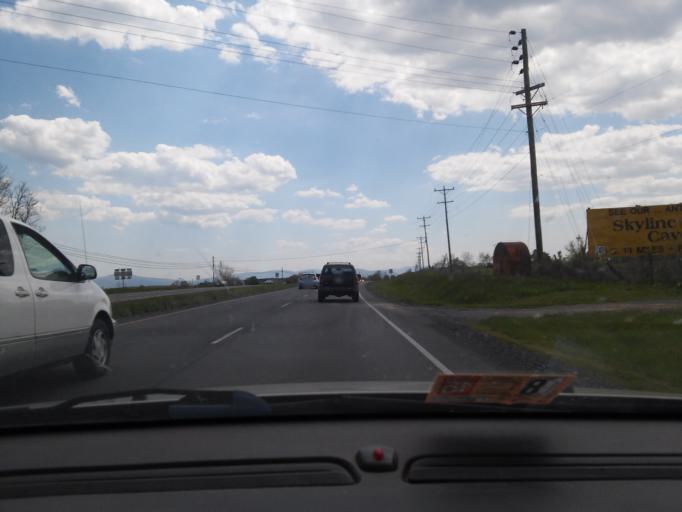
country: US
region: Virginia
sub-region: Frederick County
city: Stephens City
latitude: 39.0591
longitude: -78.1398
